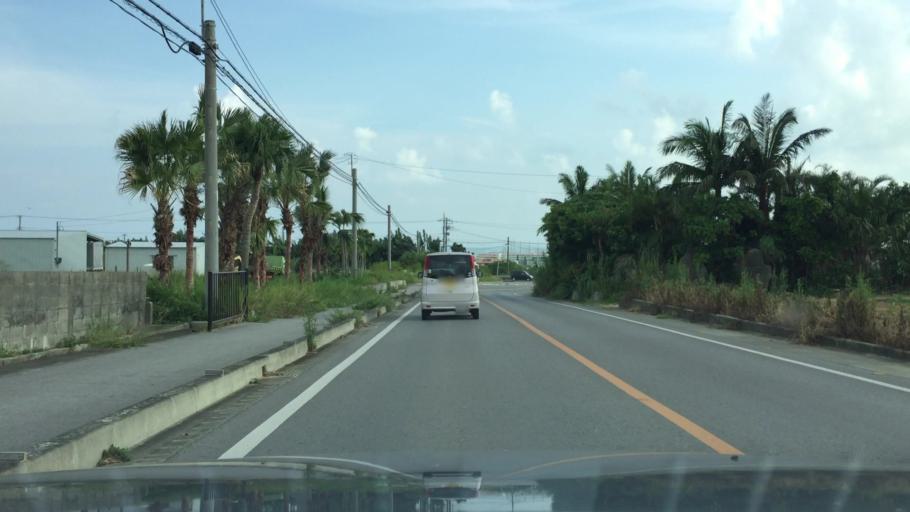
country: JP
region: Okinawa
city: Ishigaki
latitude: 24.3537
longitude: 124.1739
